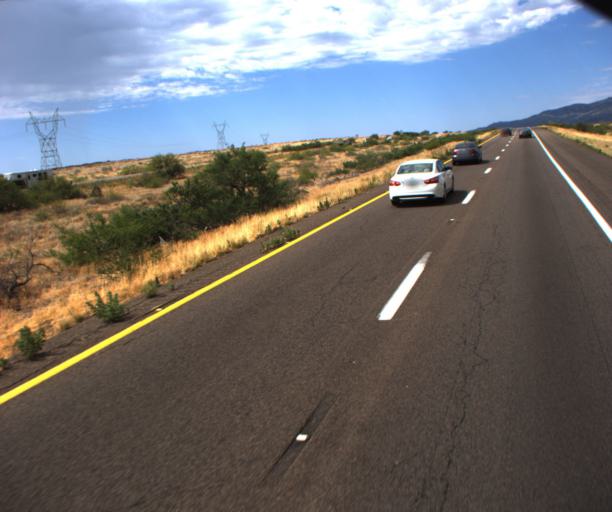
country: US
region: Arizona
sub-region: Yavapai County
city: Cordes Lakes
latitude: 34.2136
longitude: -112.1139
